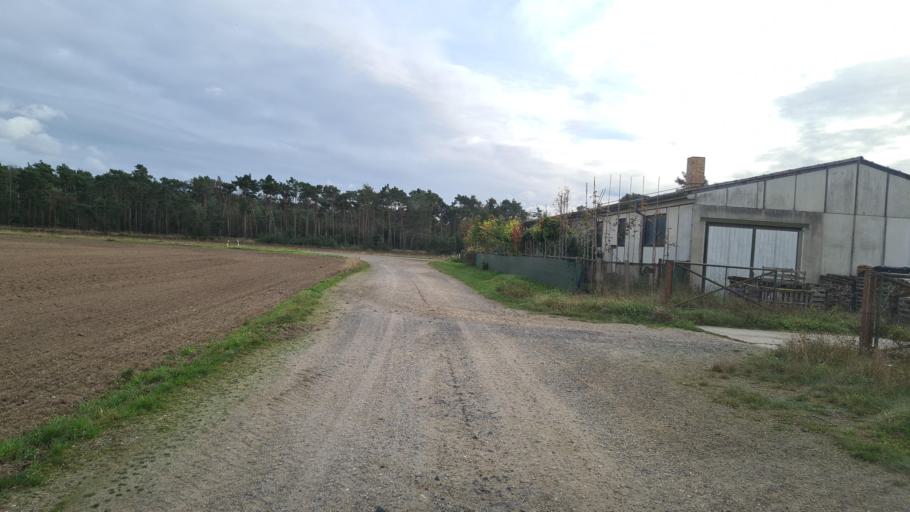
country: DE
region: Brandenburg
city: Bad Liebenwerda
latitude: 51.4732
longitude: 13.3969
